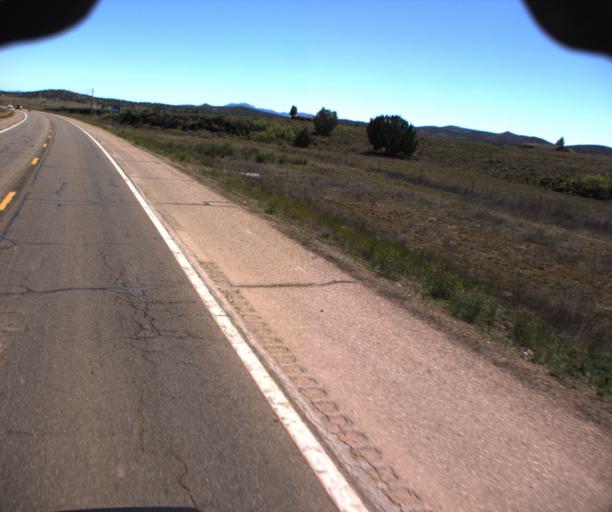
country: US
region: Arizona
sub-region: Yavapai County
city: Paulden
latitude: 34.8672
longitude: -112.4702
